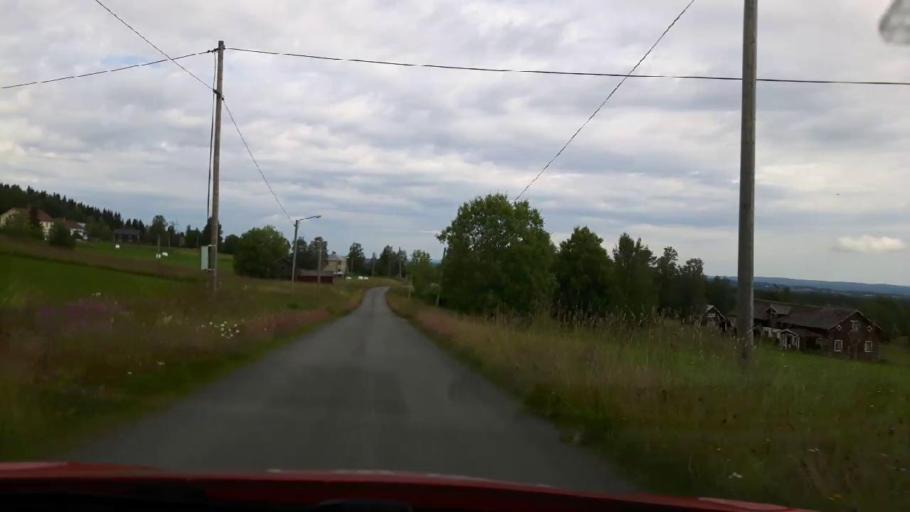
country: SE
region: Jaemtland
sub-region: OEstersunds Kommun
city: Lit
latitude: 63.3768
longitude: 15.1931
